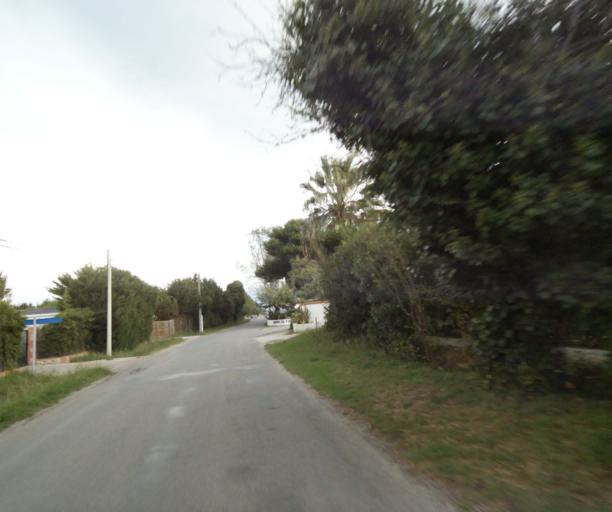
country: FR
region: Languedoc-Roussillon
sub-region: Departement des Pyrenees-Orientales
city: Argelers
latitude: 42.5695
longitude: 3.0341
